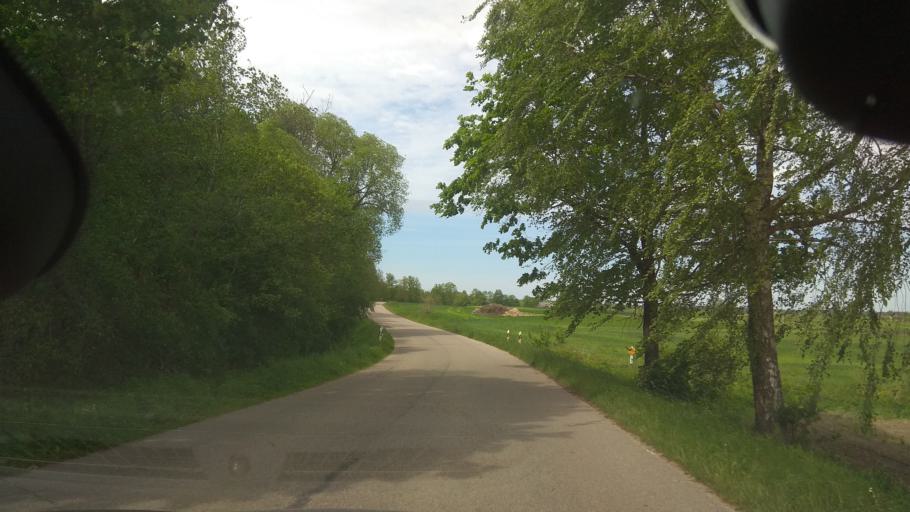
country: LT
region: Vilnius County
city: Ukmerge
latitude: 55.1514
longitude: 24.5496
